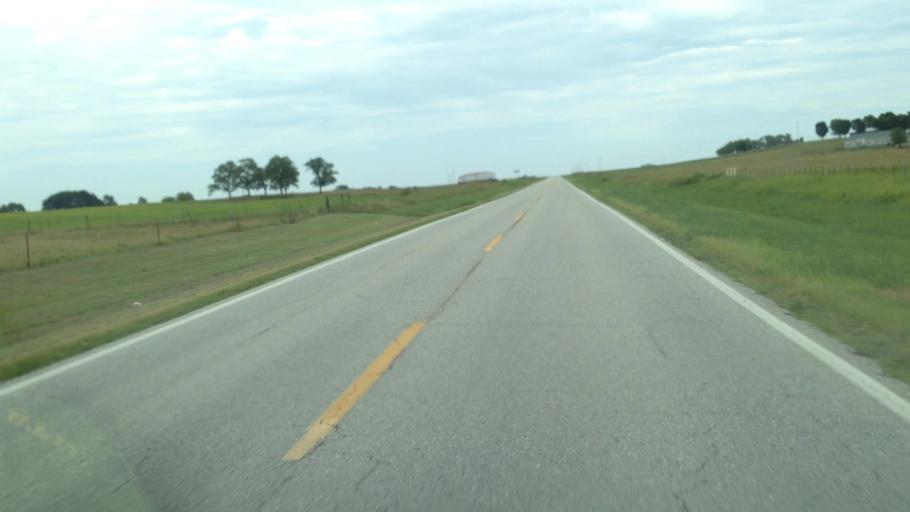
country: US
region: Oklahoma
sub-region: Craig County
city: Vinita
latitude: 36.8258
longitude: -95.1400
